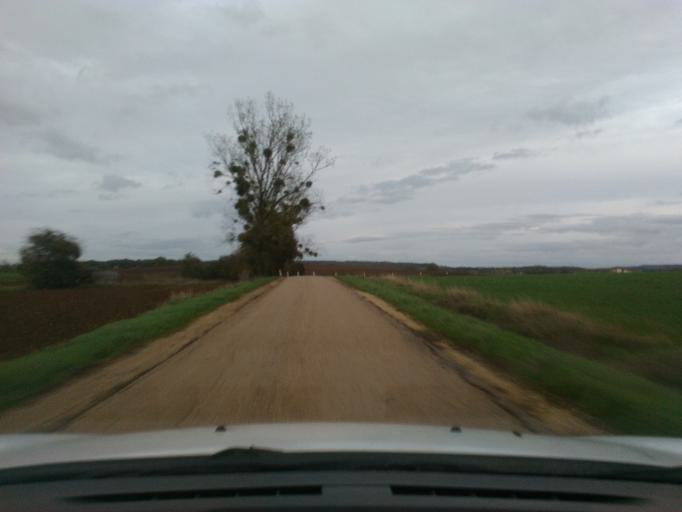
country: FR
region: Lorraine
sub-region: Departement des Vosges
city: Mirecourt
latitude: 48.3354
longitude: 6.0771
